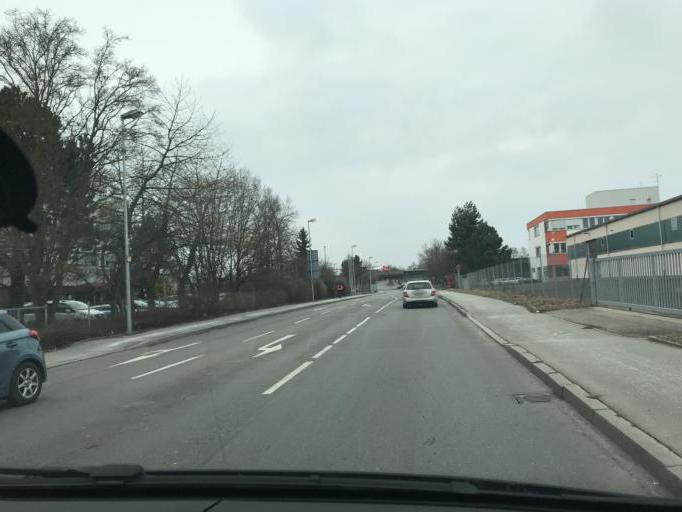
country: DE
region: Baden-Wuerttemberg
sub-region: Regierungsbezirk Stuttgart
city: Boeblingen
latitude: 48.6835
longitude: 8.9793
